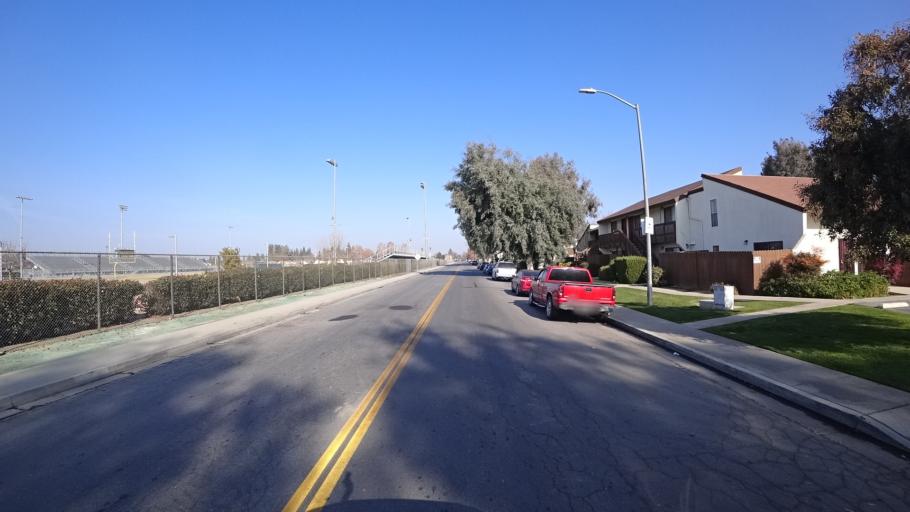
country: US
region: California
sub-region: Kern County
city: Bakersfield
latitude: 35.3421
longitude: -119.0551
